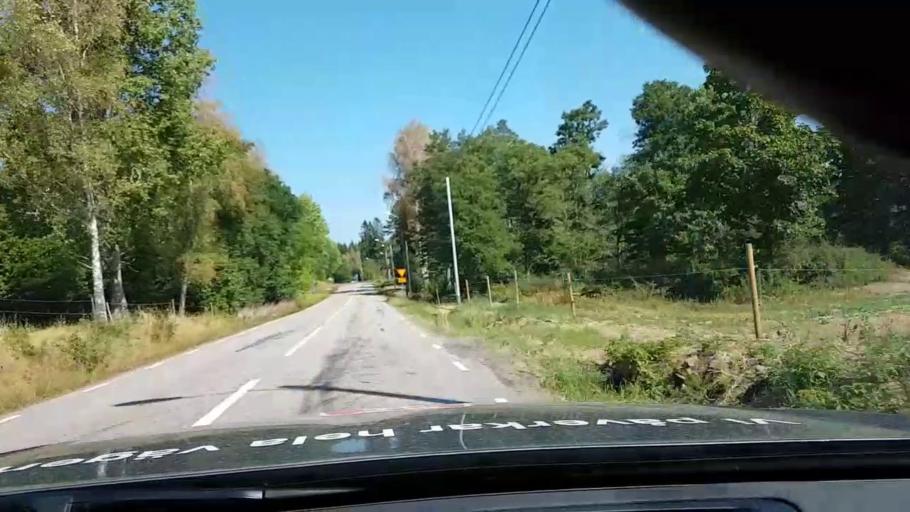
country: SE
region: Kalmar
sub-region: Hultsfreds Kommun
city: Virserum
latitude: 57.1373
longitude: 15.6597
